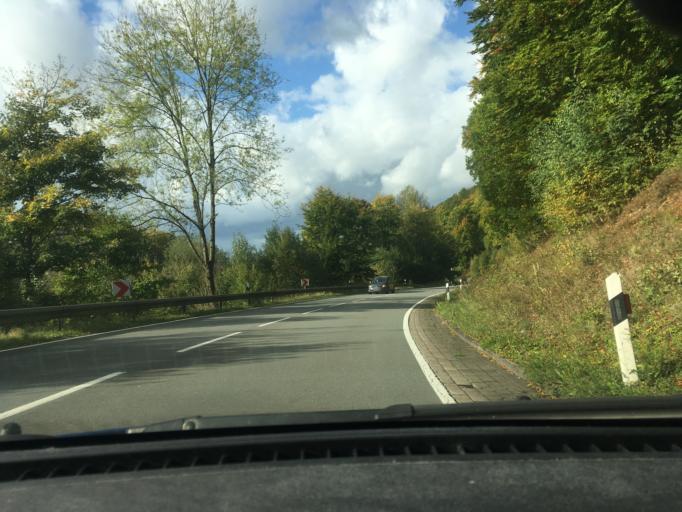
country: DE
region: Lower Saxony
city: Bevern
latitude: 51.8151
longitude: 9.4907
